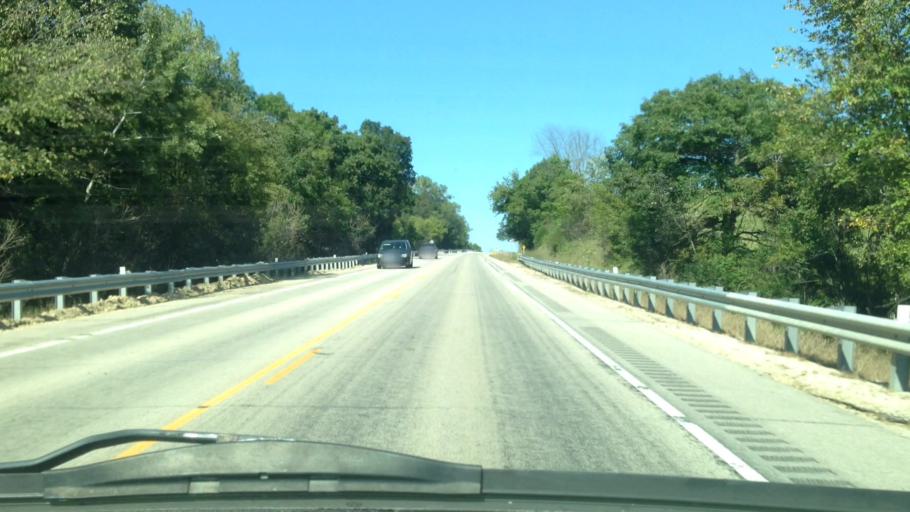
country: US
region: Minnesota
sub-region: Fillmore County
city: Rushford
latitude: 43.8485
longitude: -91.7510
